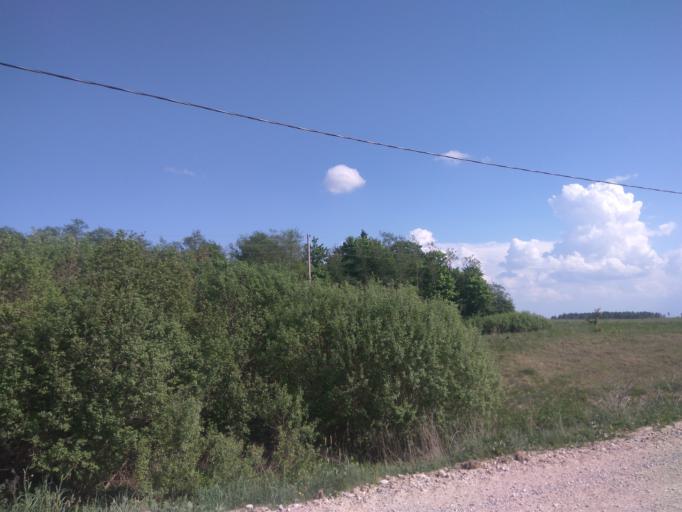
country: LV
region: Kuldigas Rajons
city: Kuldiga
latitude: 57.1635
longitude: 22.0189
